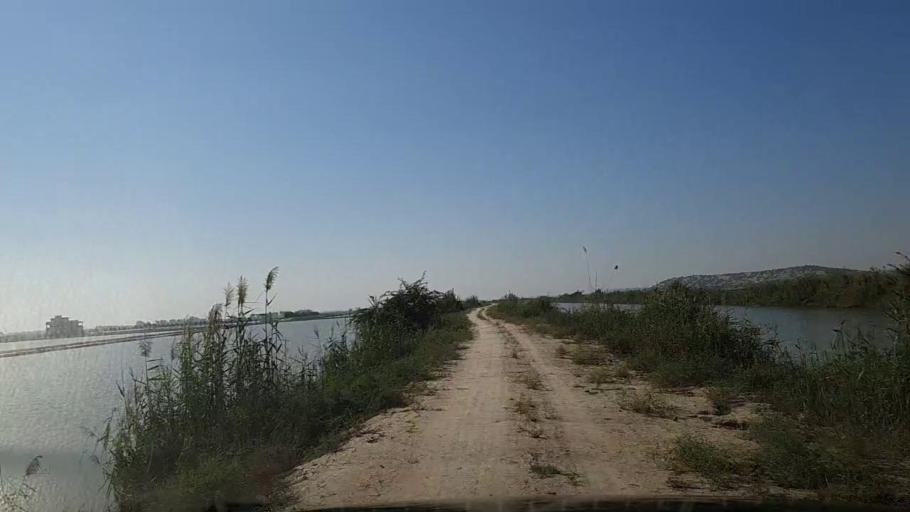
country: PK
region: Sindh
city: Thatta
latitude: 24.6841
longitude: 67.8917
